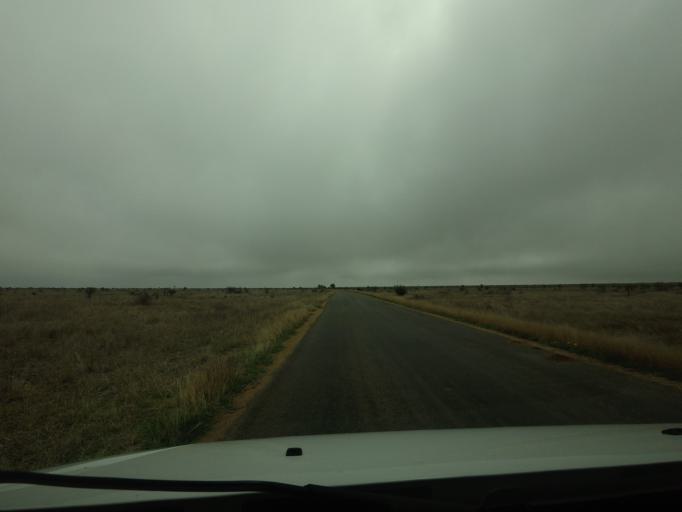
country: ZA
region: Limpopo
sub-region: Mopani District Municipality
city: Phalaborwa
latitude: -24.2325
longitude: 31.7206
